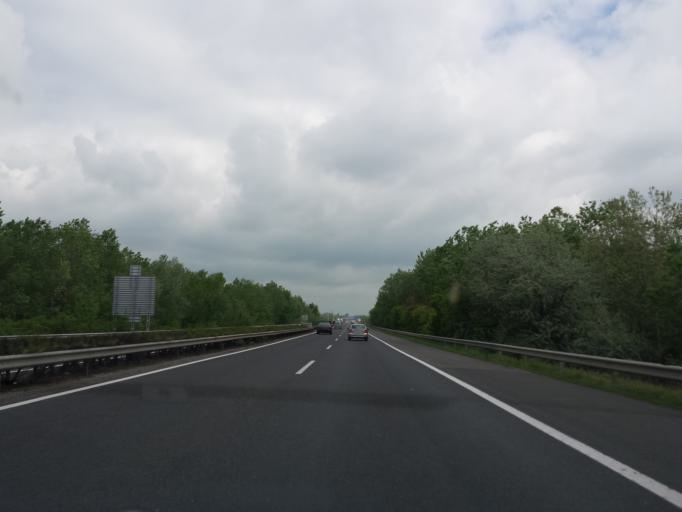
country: HU
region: Gyor-Moson-Sopron
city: Gyorujbarat
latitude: 47.6351
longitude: 17.6799
